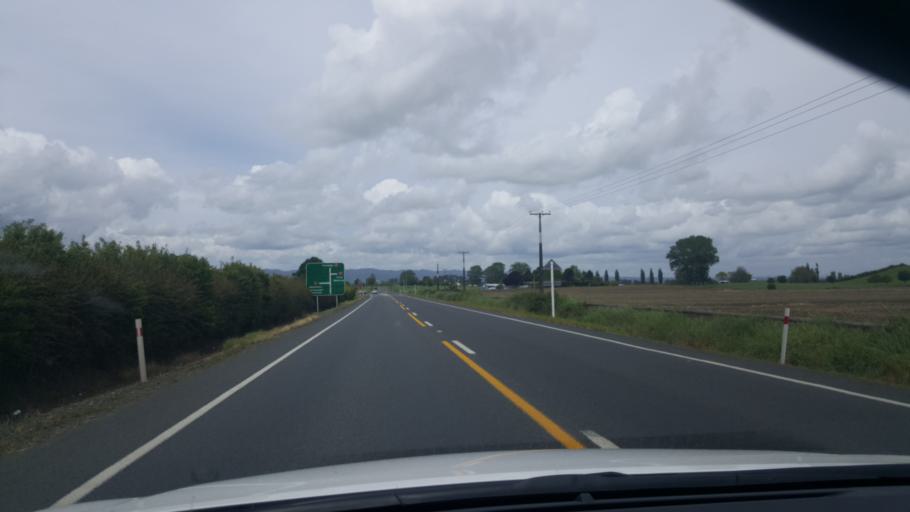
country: NZ
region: Waikato
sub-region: Matamata-Piako District
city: Matamata
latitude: -37.8872
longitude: 175.7714
